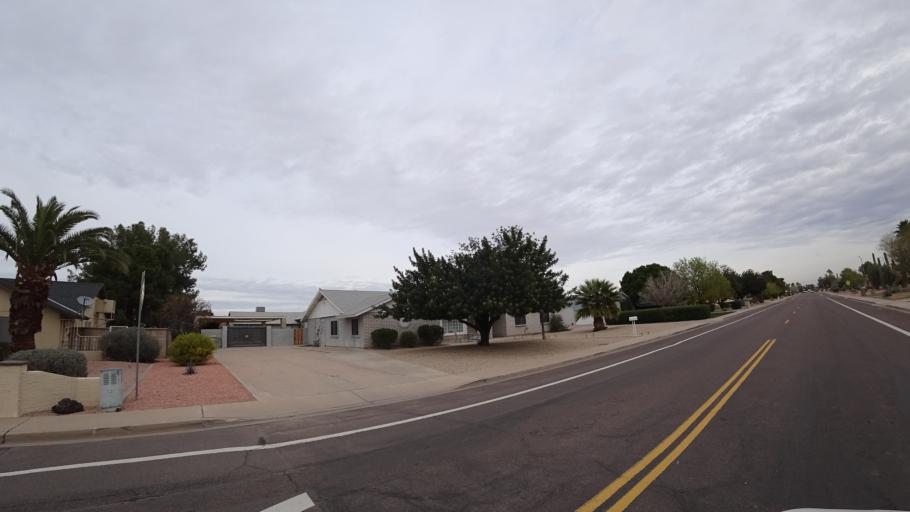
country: US
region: Arizona
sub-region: Maricopa County
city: Peoria
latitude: 33.6470
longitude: -112.1921
